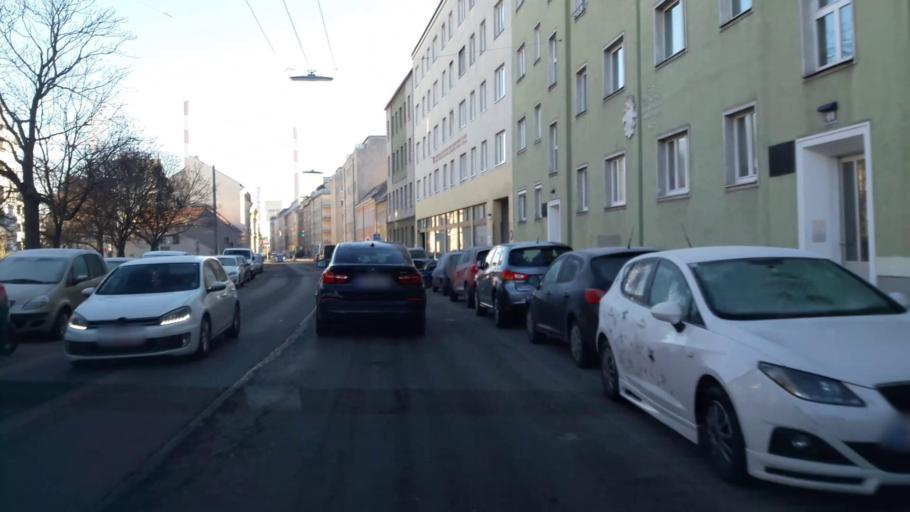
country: AT
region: Vienna
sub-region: Wien Stadt
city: Vienna
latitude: 48.1789
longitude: 16.4185
